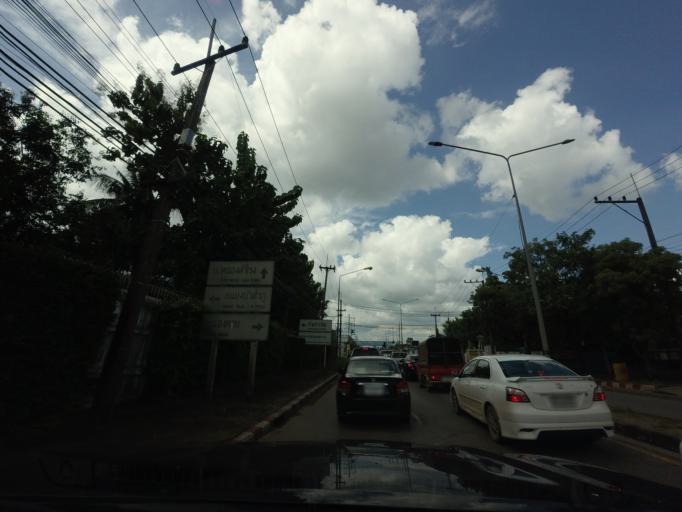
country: TH
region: Changwat Udon Thani
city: Udon Thani
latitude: 17.4246
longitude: 102.7769
